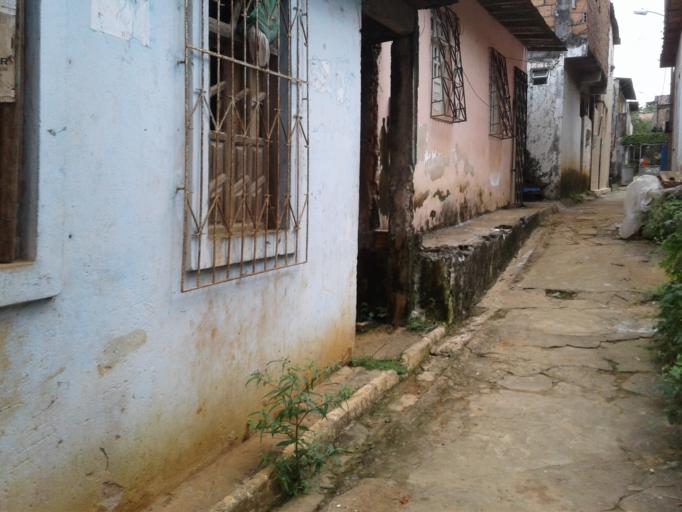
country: BR
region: Bahia
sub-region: Salvador
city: Salvador
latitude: -12.9086
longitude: -38.4731
